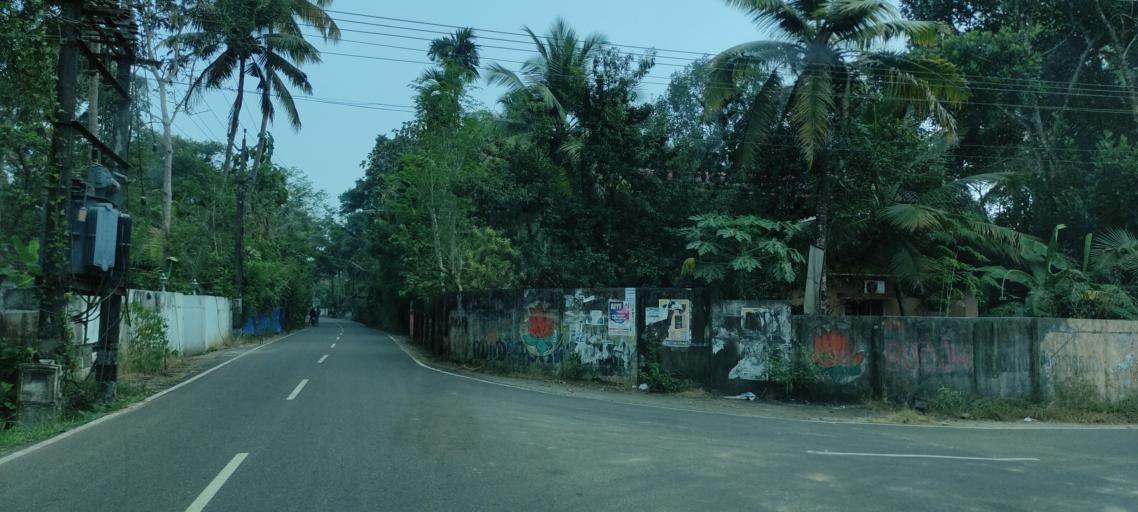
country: IN
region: Kerala
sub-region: Alappuzha
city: Shertallai
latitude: 9.5881
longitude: 76.3416
